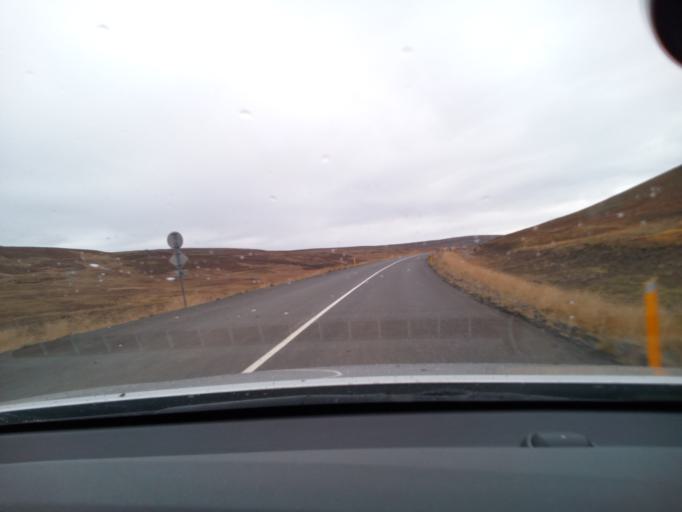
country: IS
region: Northeast
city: Laugar
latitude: 65.7966
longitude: -17.2427
